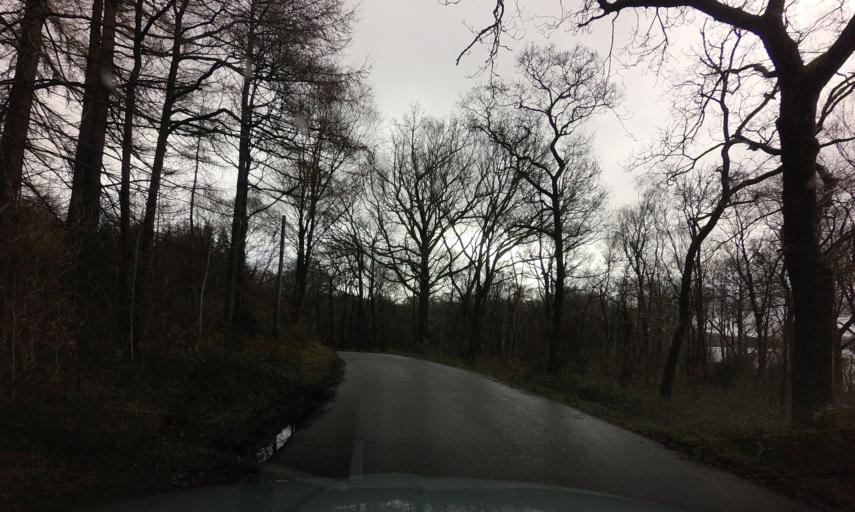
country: GB
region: Scotland
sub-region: West Dunbartonshire
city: Balloch
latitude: 56.1268
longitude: -4.6057
